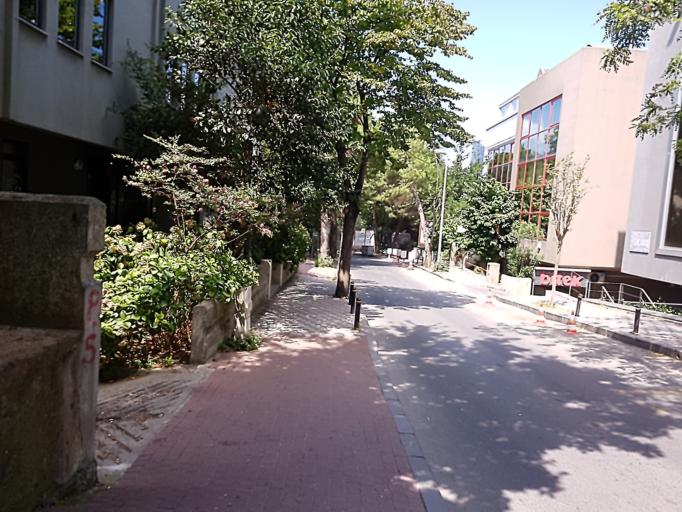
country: TR
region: Istanbul
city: Sisli
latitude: 41.0702
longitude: 29.0098
